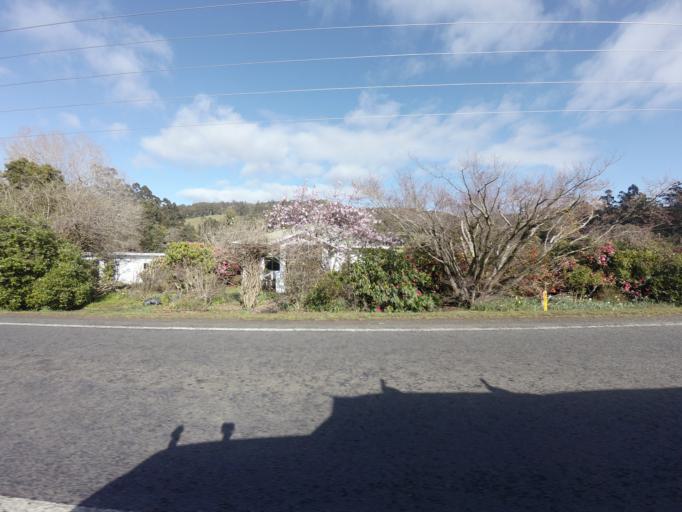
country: AU
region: Tasmania
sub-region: Huon Valley
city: Cygnet
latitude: -43.2889
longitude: 147.0106
